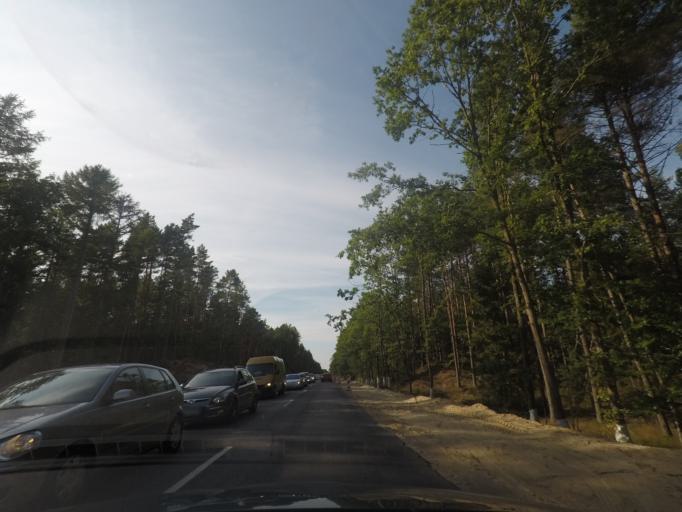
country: PL
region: Pomeranian Voivodeship
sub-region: Powiat leborski
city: Leba
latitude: 54.7051
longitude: 17.5840
